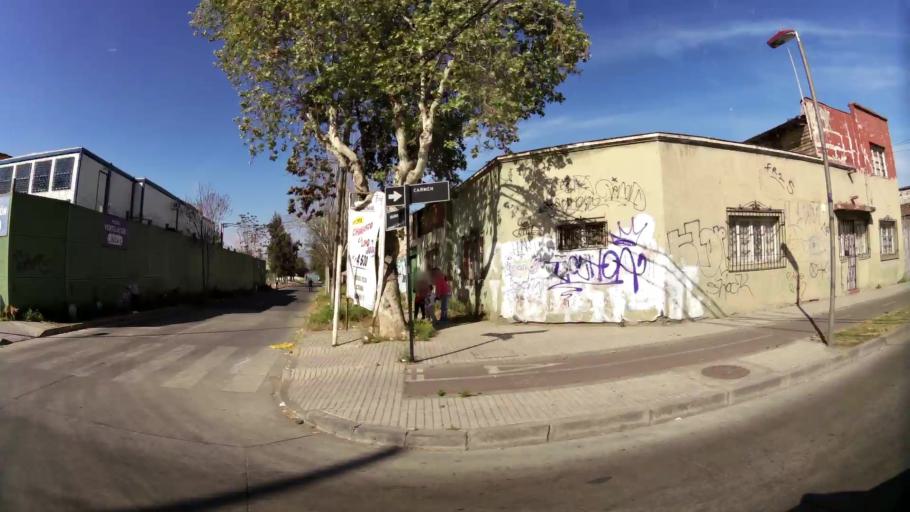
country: CL
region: Santiago Metropolitan
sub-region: Provincia de Santiago
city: Santiago
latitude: -33.4750
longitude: -70.6349
